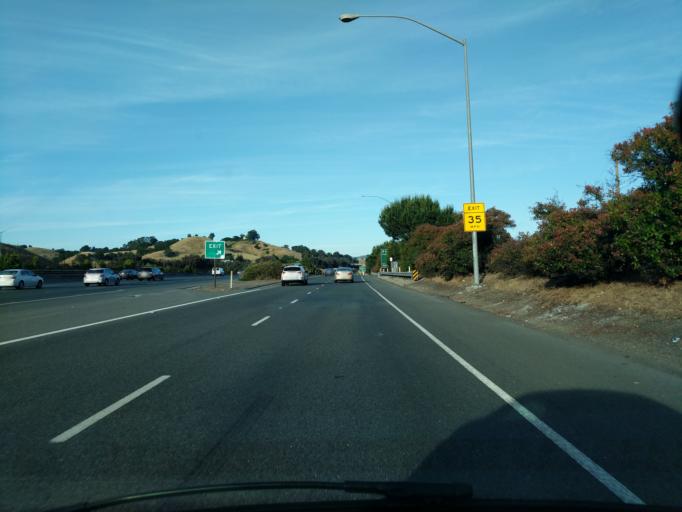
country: US
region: California
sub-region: Contra Costa County
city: Lafayette
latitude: 37.8970
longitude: -122.1003
